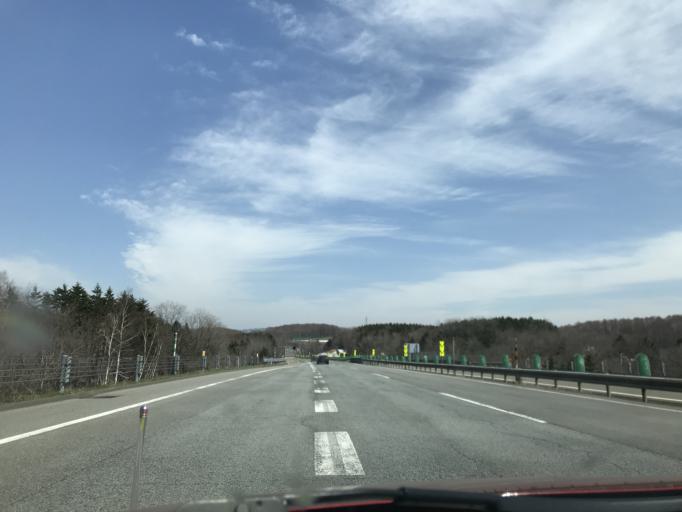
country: JP
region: Hokkaido
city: Iwamizawa
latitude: 43.1978
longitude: 141.8070
